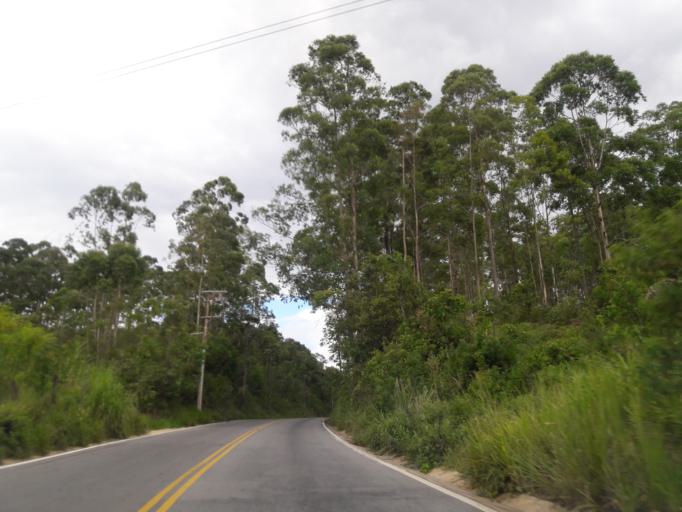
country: BR
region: Sao Paulo
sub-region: Aruja
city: Aruja
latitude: -23.3756
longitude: -46.4194
